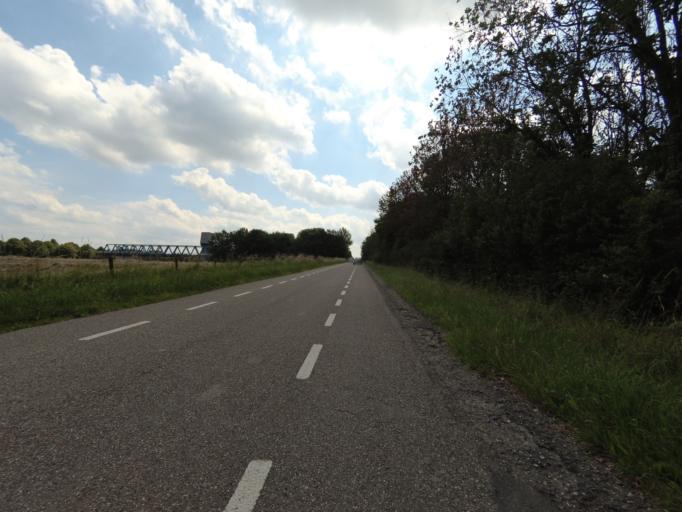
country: NL
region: Utrecht
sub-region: Gemeente Wijk bij Duurstede
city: Wijk bij Duurstede
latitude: 51.9542
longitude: 5.3523
